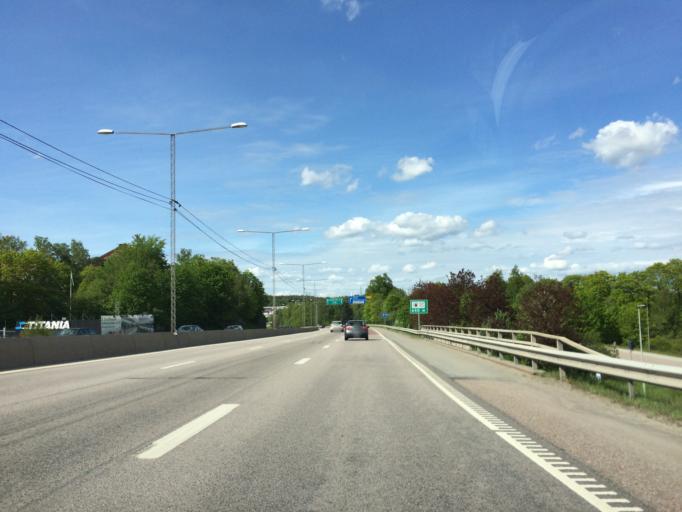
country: SE
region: Stockholm
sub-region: Danderyds Kommun
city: Djursholm
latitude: 59.4030
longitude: 18.0372
